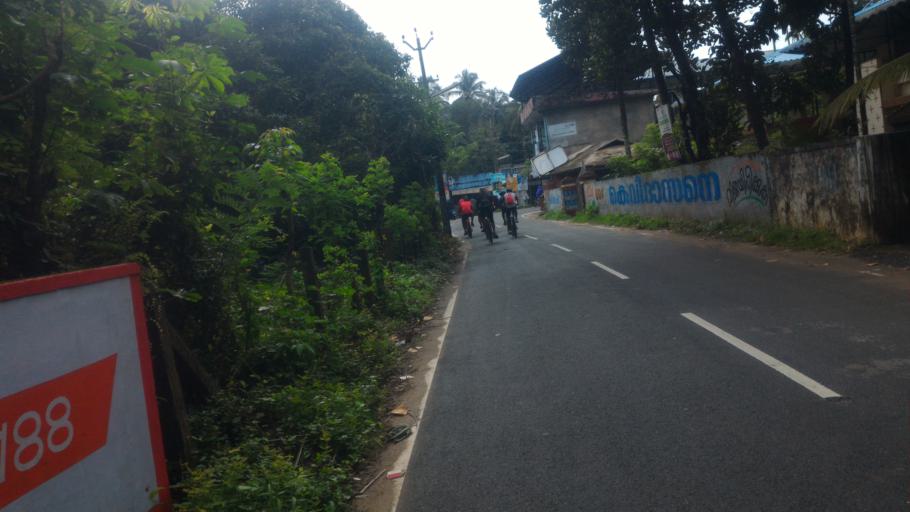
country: IN
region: Kerala
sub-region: Thrissur District
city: Thanniyam
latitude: 10.4386
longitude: 76.0836
